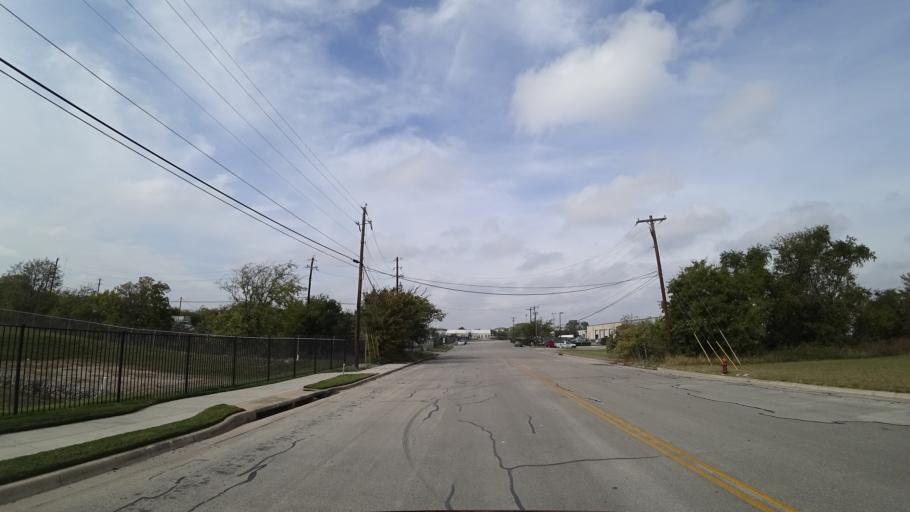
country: US
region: Texas
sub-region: Travis County
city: Windemere
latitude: 30.4525
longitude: -97.6568
